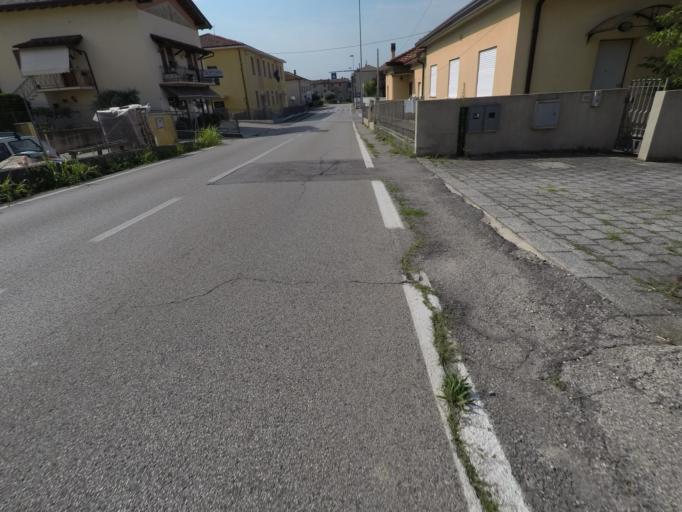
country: IT
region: Veneto
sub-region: Provincia di Treviso
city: Carpesica
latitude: 45.9482
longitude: 12.2917
